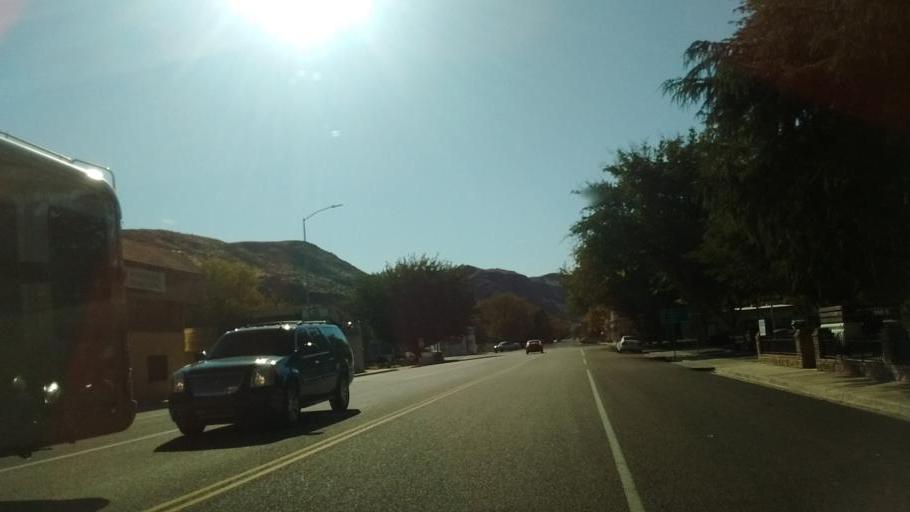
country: US
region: Utah
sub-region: Washington County
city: Hurricane
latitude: 37.1762
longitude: -113.2882
